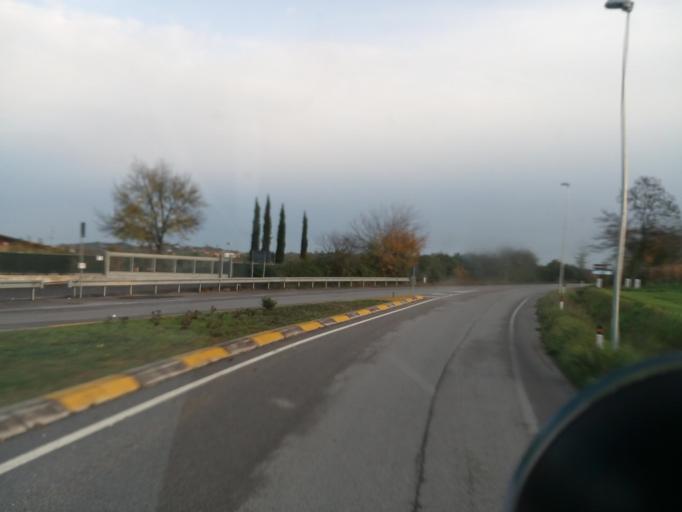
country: IT
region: Lombardy
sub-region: Provincia di Brescia
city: San Martino della Battaglia
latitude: 45.4255
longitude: 10.6091
